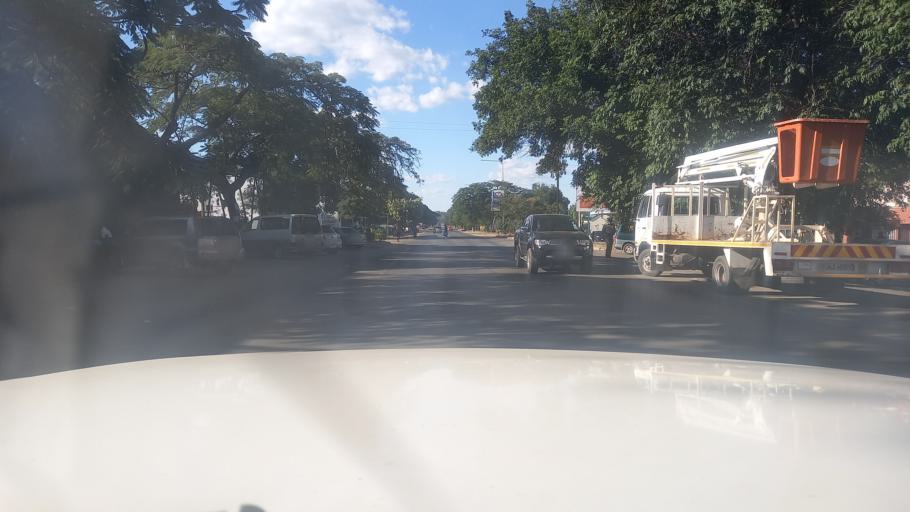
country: ZM
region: Southern
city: Livingstone
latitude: -17.8442
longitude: 25.8597
